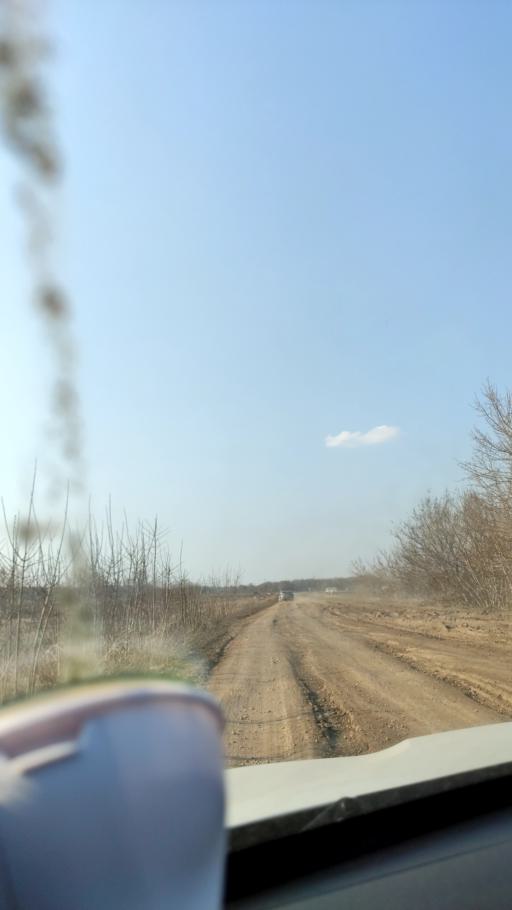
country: RU
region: Samara
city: Kinel'
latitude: 53.2586
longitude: 50.5275
